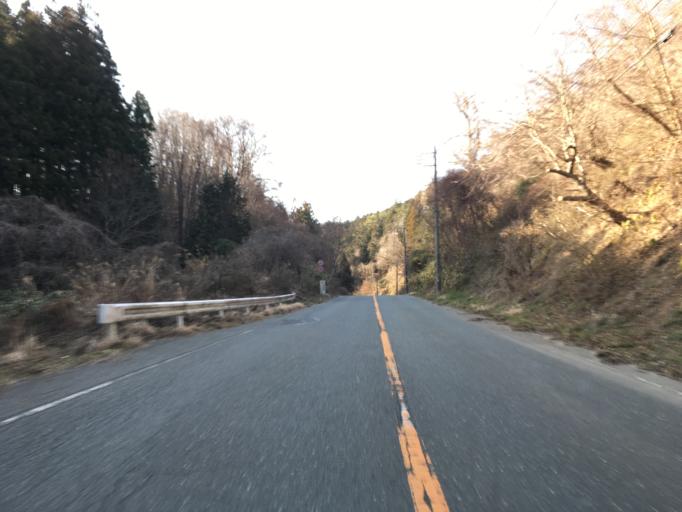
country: JP
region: Ibaraki
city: Daigo
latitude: 36.7350
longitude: 140.5232
